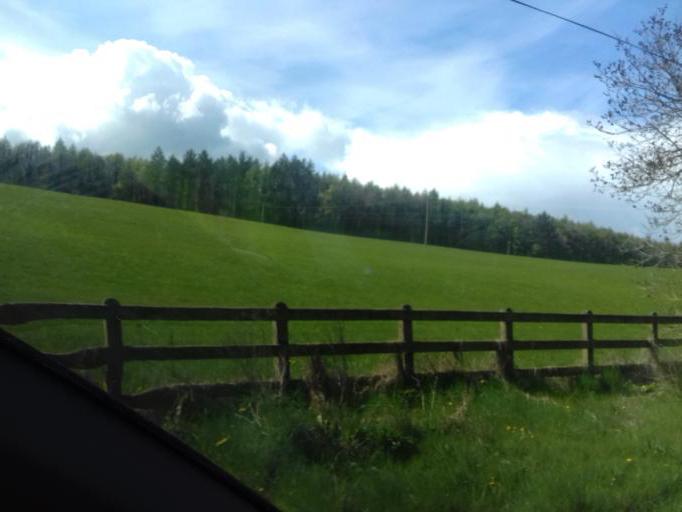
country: GB
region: Northern Ireland
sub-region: Fermanagh District
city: Enniskillen
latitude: 54.4092
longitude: -7.7223
